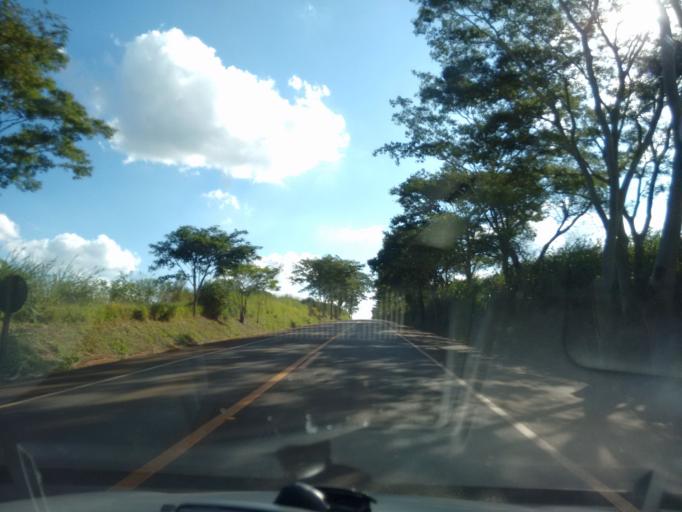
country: BR
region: Sao Paulo
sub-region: Americo Brasiliense
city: Americo Brasiliense
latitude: -21.6231
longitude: -47.9855
